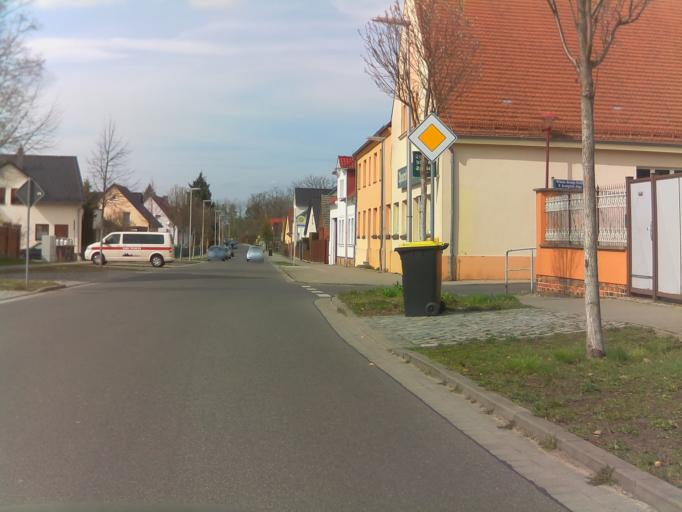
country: DE
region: Brandenburg
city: Cottbus
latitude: 51.7584
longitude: 14.3003
